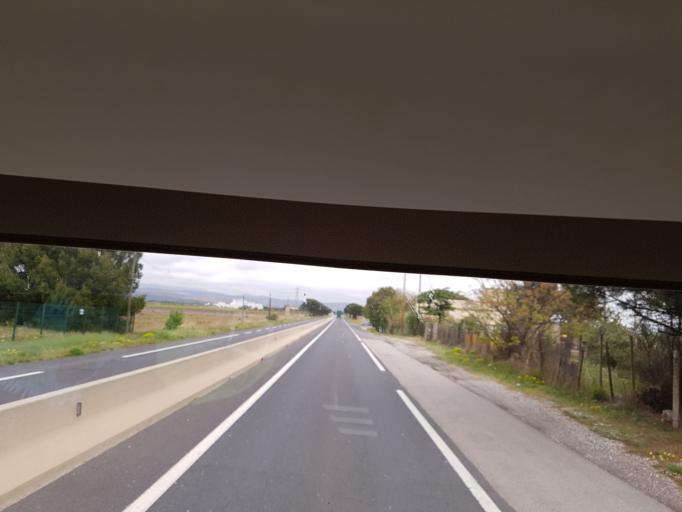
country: FR
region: Languedoc-Roussillon
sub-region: Departement des Pyrenees-Orientales
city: Rivesaltes
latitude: 42.7924
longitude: 2.9075
